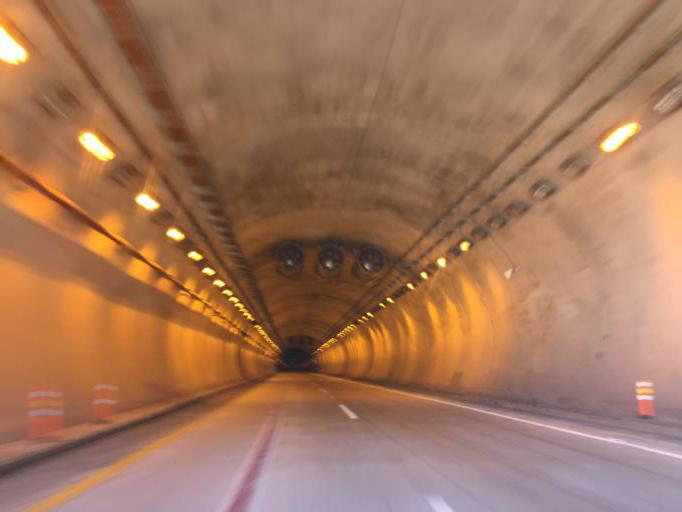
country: MX
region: Puebla
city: Xicotepec de Juarez
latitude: 20.2876
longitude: -97.9717
